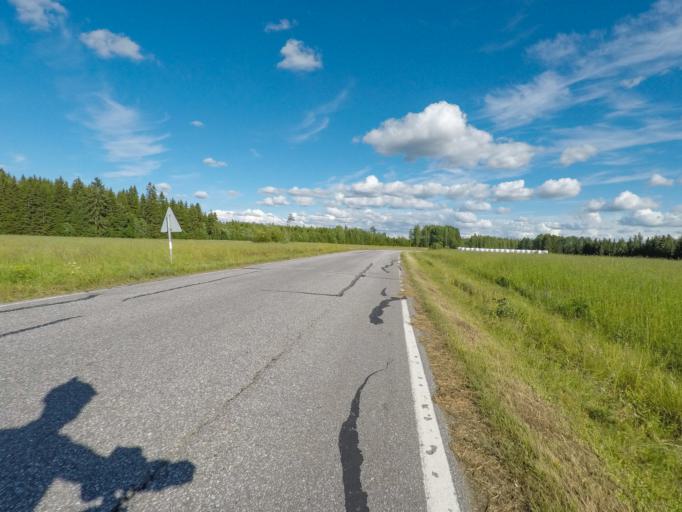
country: FI
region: South Karelia
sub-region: Imatra
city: Imatra
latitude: 61.1366
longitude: 28.6533
